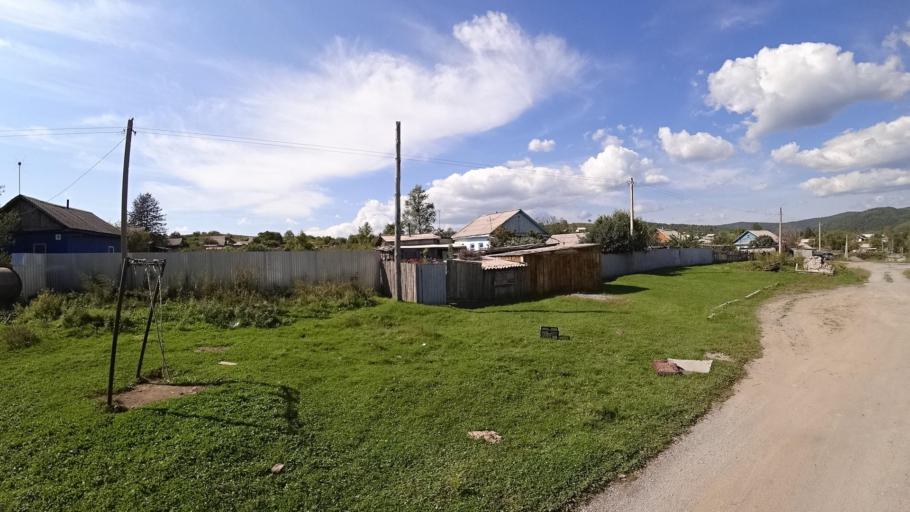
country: RU
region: Jewish Autonomous Oblast
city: Londoko
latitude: 49.0085
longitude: 131.8719
